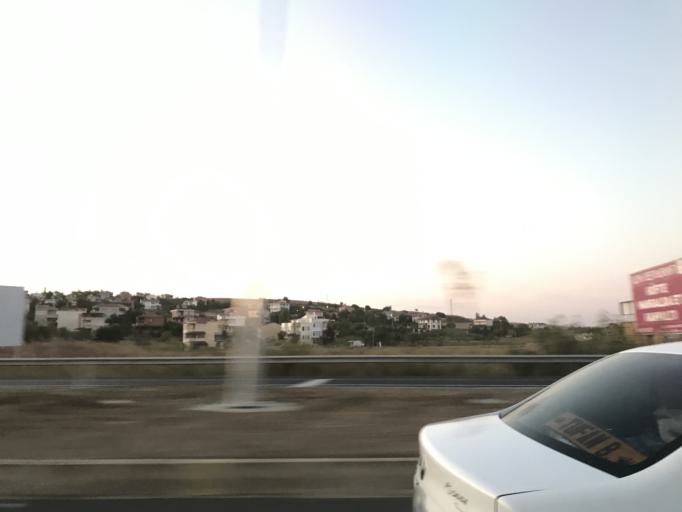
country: TR
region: Tekirdag
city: Tekirdag
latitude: 41.0038
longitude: 27.6788
